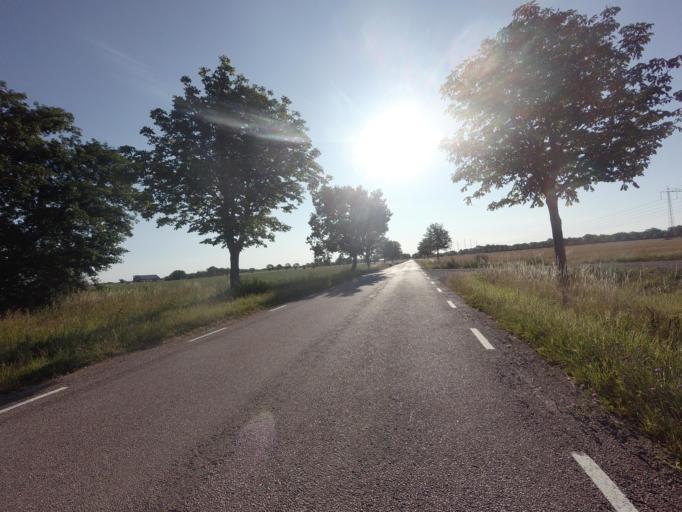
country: SE
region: Skane
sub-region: Hoganas Kommun
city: Hoganas
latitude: 56.1376
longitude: 12.6080
